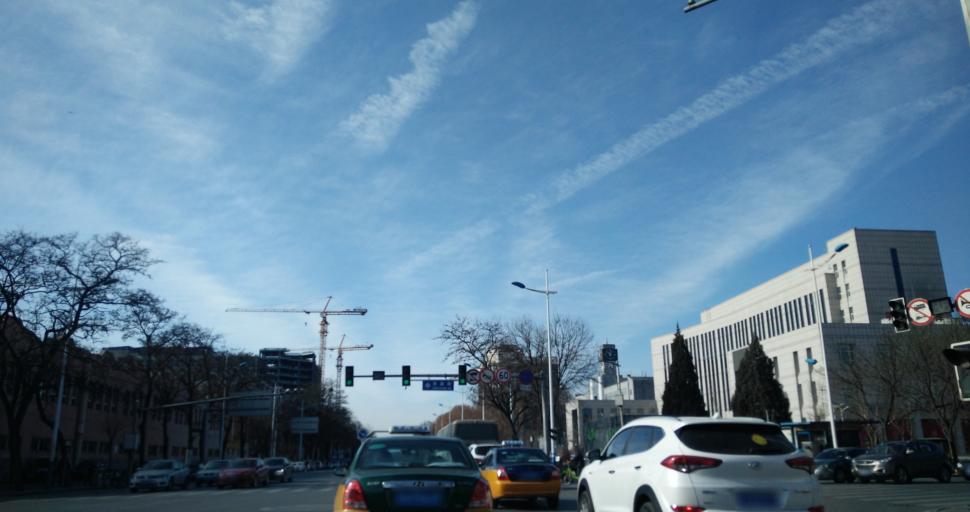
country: CN
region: Beijing
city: Daxing
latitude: 39.7412
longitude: 116.3371
